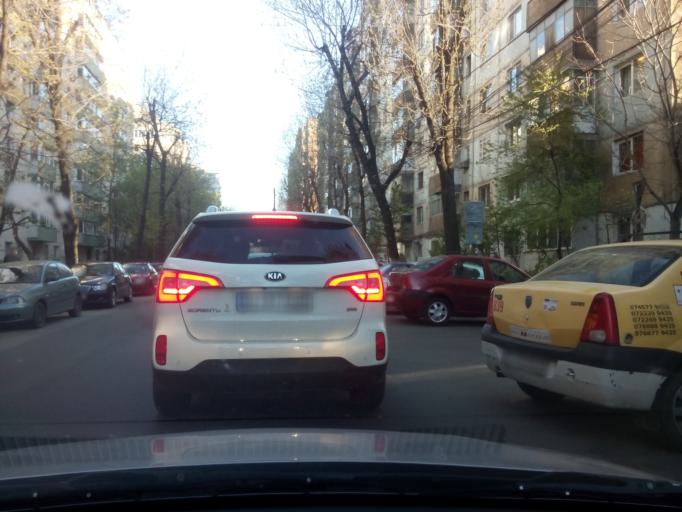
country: RO
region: Bucuresti
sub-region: Municipiul Bucuresti
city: Bucharest
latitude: 44.4637
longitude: 26.1182
